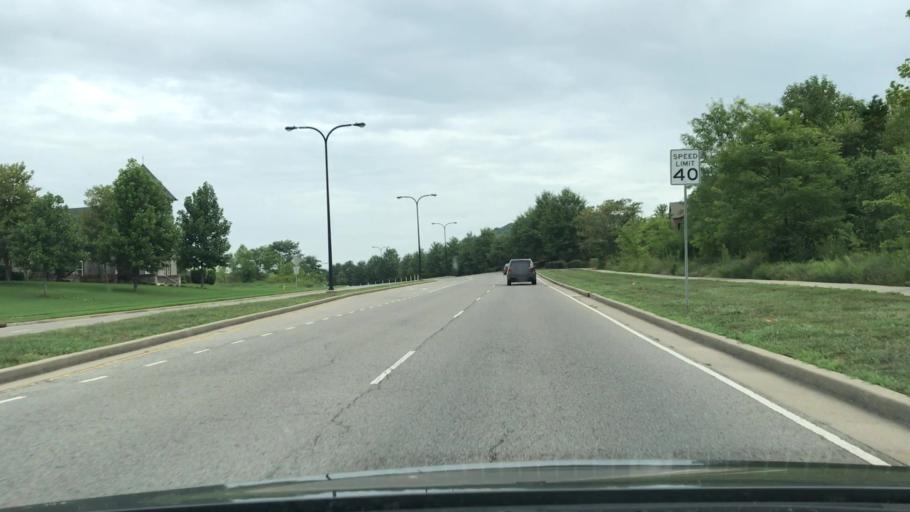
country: US
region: Tennessee
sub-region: Williamson County
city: Franklin
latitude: 35.9328
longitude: -86.7942
